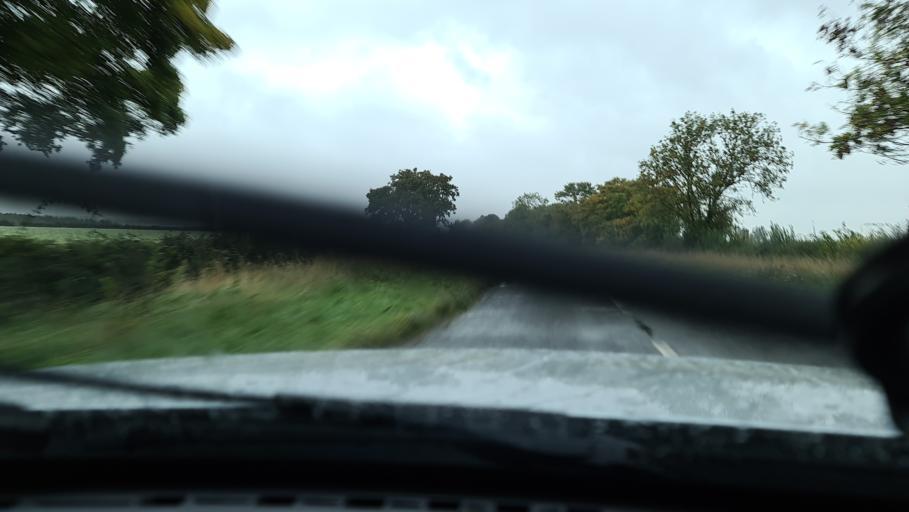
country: GB
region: England
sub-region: Oxfordshire
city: Woodstock
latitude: 51.8832
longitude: -1.3692
